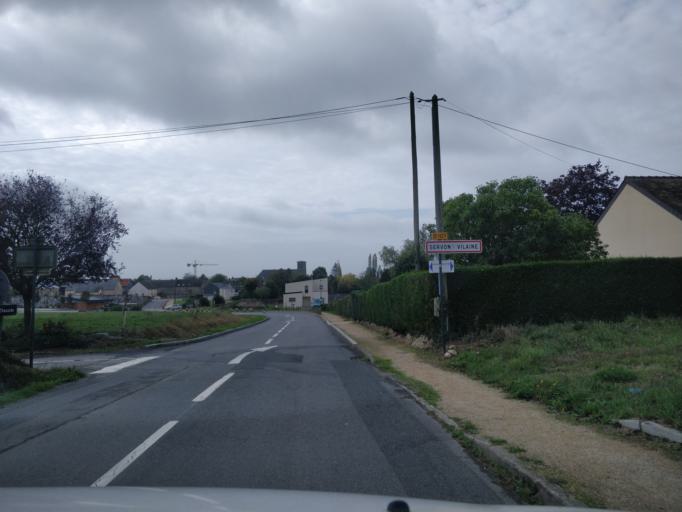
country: FR
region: Brittany
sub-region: Departement d'Ille-et-Vilaine
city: Servon-sur-Vilaine
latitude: 48.1261
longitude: -1.4587
